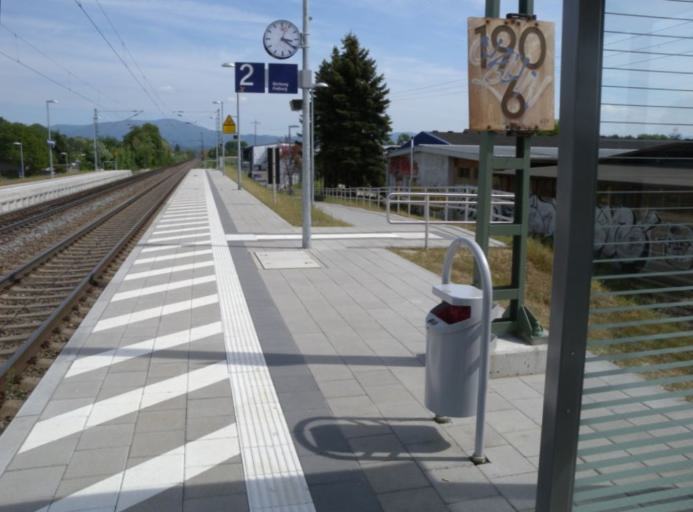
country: DE
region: Baden-Wuerttemberg
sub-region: Freiburg Region
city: Teningen
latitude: 48.1287
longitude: 7.8245
